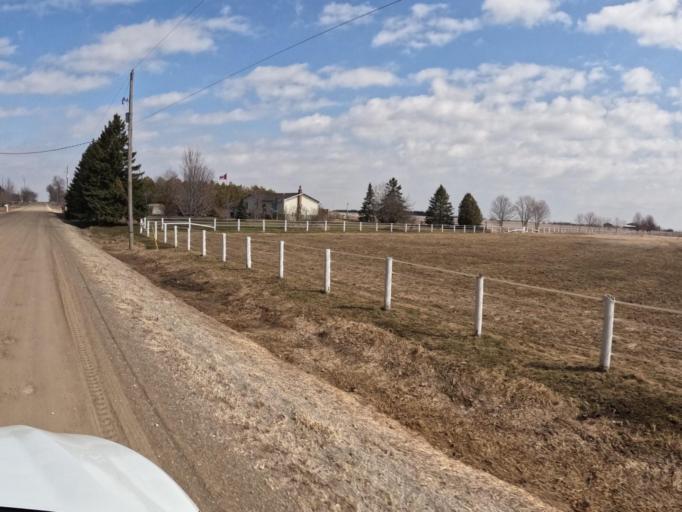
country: CA
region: Ontario
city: Orangeville
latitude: 43.9093
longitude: -80.2529
